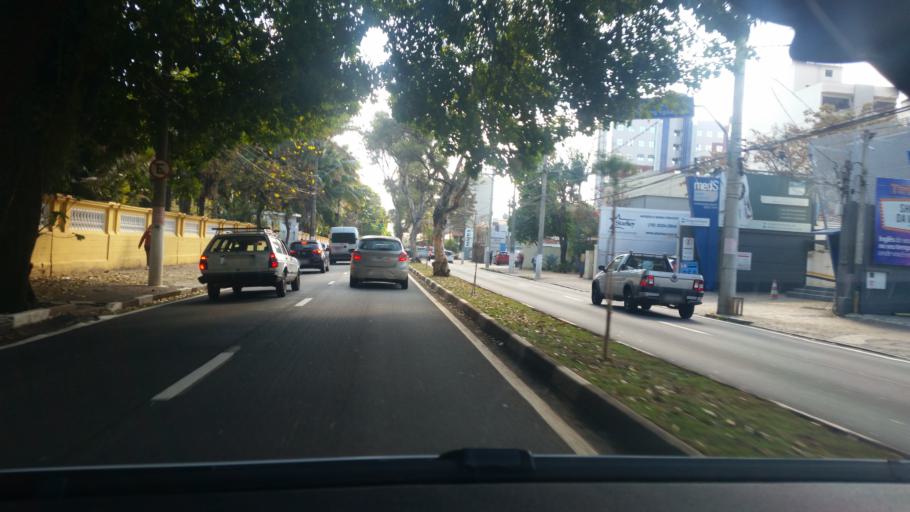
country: BR
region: Sao Paulo
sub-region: Campinas
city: Campinas
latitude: -22.8939
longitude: -47.0654
